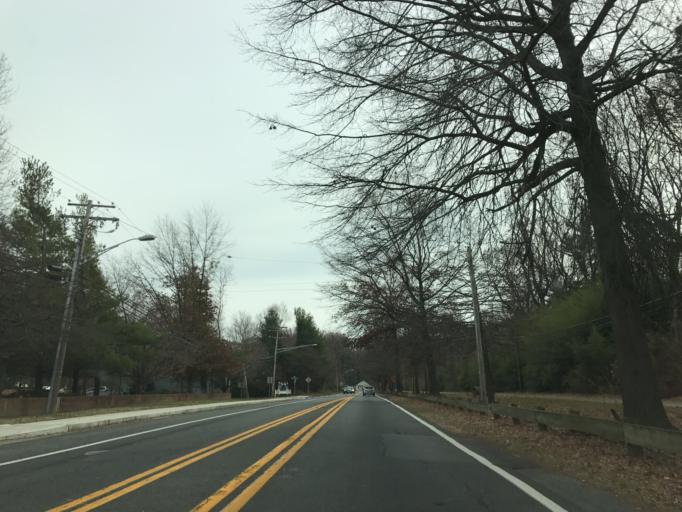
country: US
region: Maryland
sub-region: Anne Arundel County
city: Severna Park
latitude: 39.0695
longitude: -76.5448
